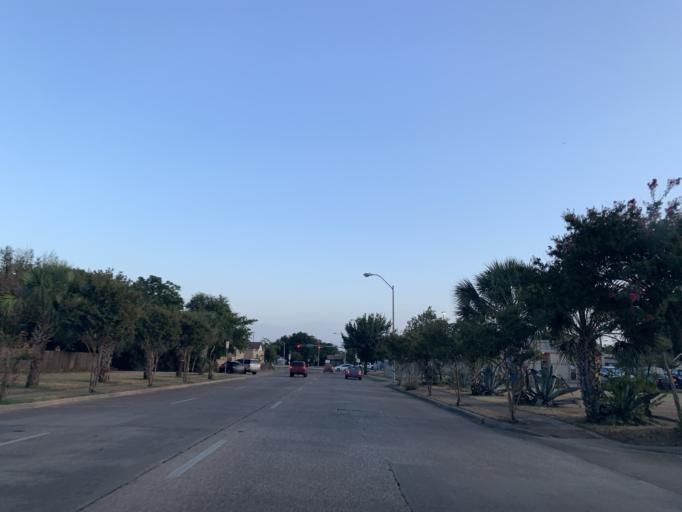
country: US
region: Texas
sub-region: Dallas County
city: Cockrell Hill
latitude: 32.7424
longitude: -96.8395
